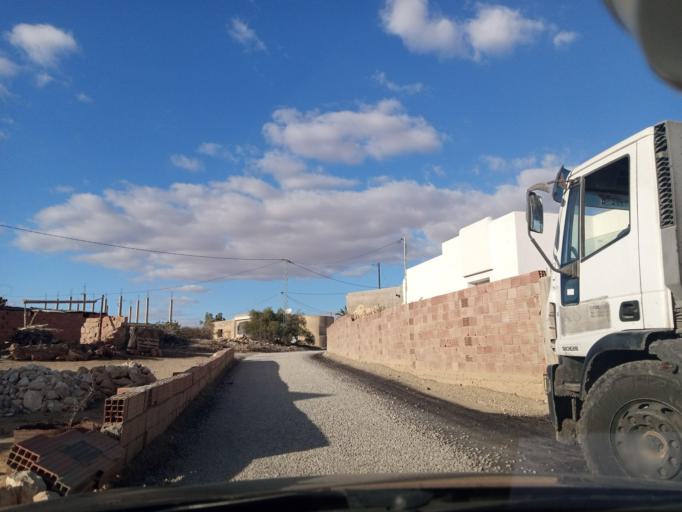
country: TN
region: Safaqis
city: Bi'r `Ali Bin Khalifah
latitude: 34.7117
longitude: 10.4226
